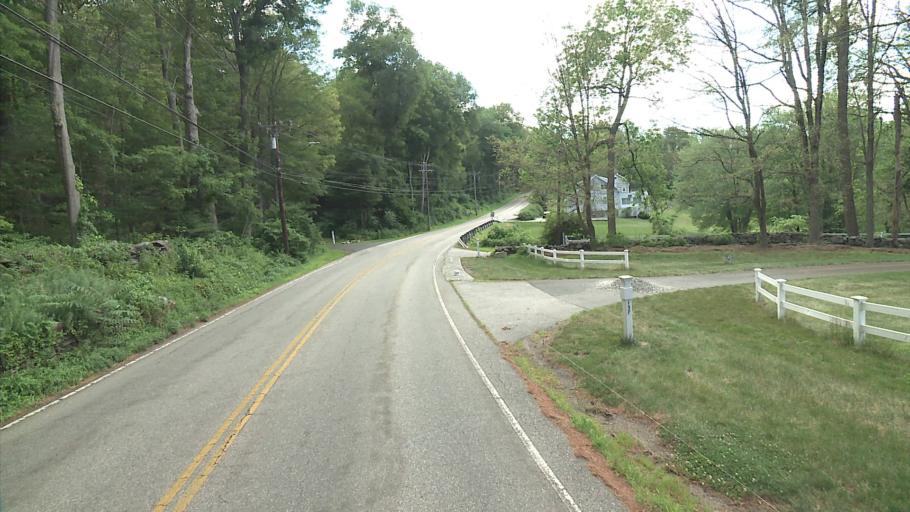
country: US
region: Connecticut
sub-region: Middlesex County
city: Higganum
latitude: 41.5449
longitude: -72.5453
